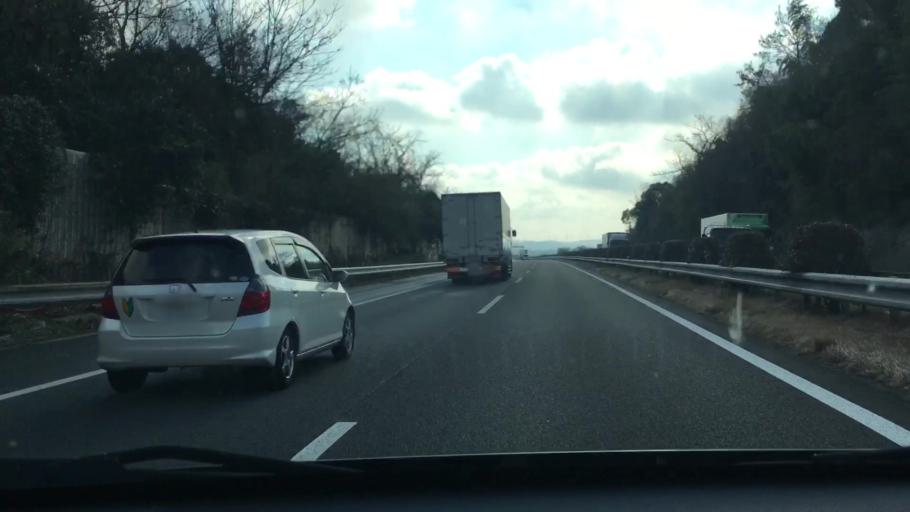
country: JP
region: Kumamoto
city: Uto
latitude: 32.7249
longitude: 130.7720
